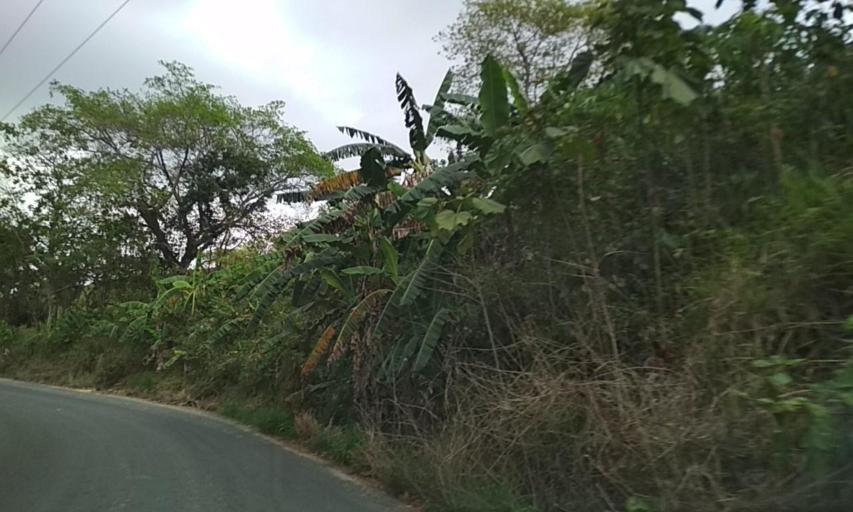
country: MX
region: Tabasco
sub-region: Huimanguillo
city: Francisco Rueda
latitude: 17.6270
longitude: -94.0897
